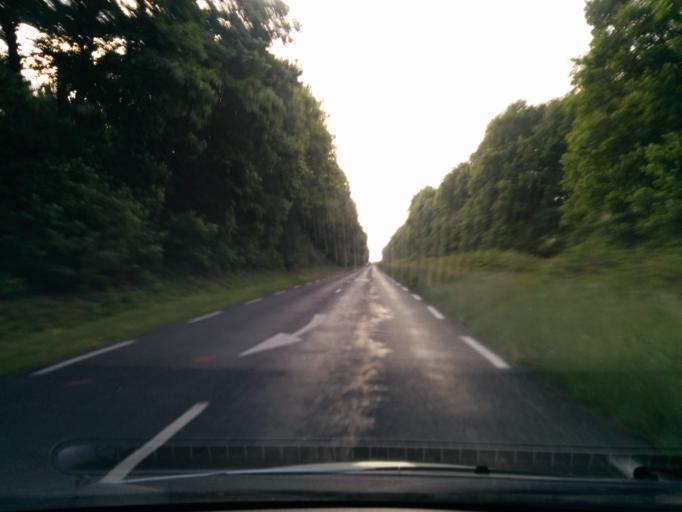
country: FR
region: Ile-de-France
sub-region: Departement des Yvelines
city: Limetz-Villez
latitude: 49.0970
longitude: 1.5150
